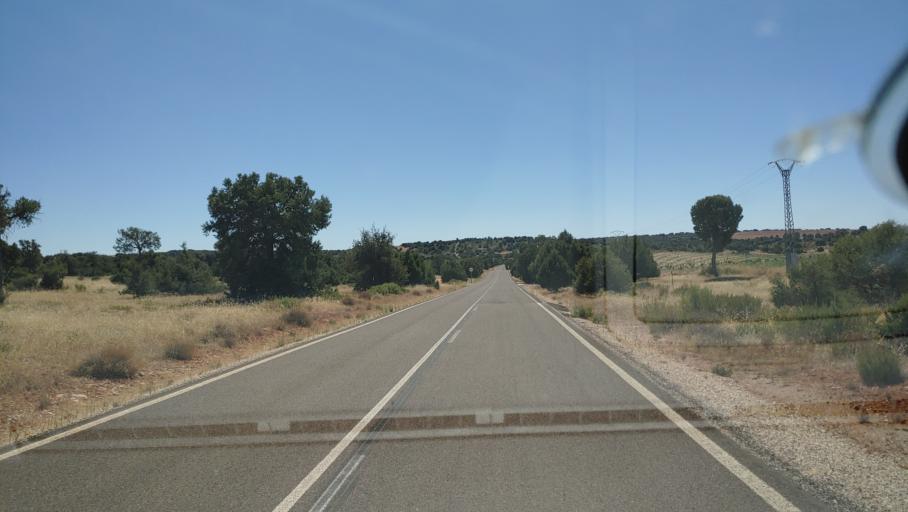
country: ES
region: Castille-La Mancha
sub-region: Provincia de Albacete
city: Ossa de Montiel
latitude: 38.8579
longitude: -2.8018
